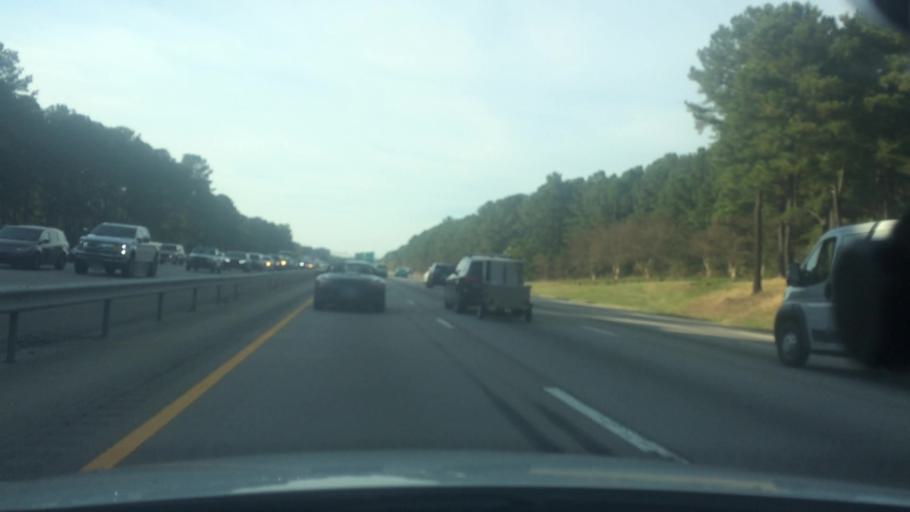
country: US
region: North Carolina
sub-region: Wake County
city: Morrisville
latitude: 35.8617
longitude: -78.8151
